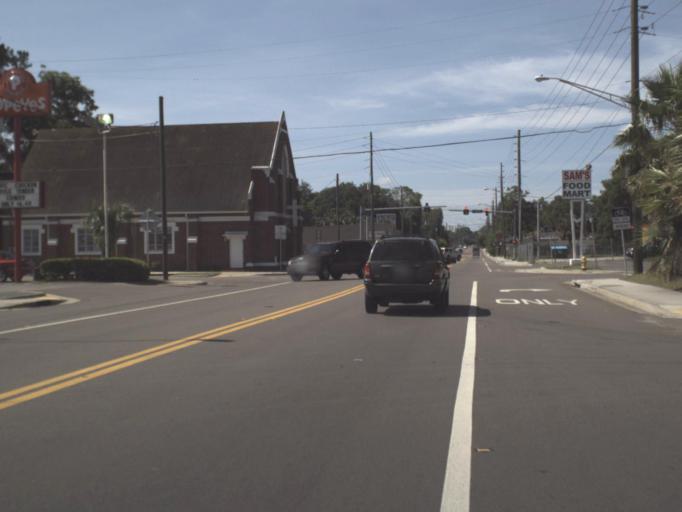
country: US
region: Florida
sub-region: Duval County
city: Jacksonville
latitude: 30.3203
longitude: -81.7055
